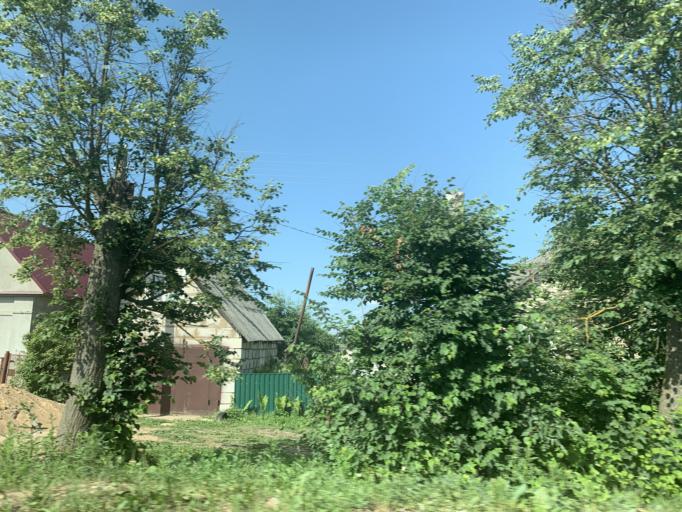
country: BY
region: Minsk
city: Dzyarzhynsk
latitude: 53.6991
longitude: 27.1015
